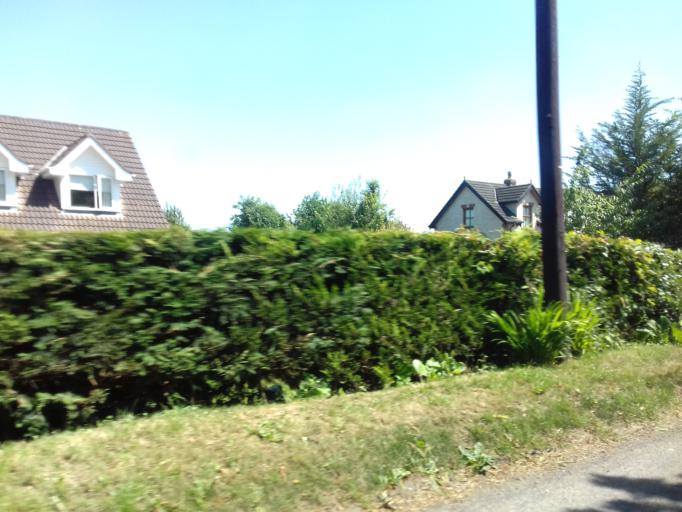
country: IE
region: Leinster
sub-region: An Mhi
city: Ashbourne
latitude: 53.5358
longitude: -6.3240
